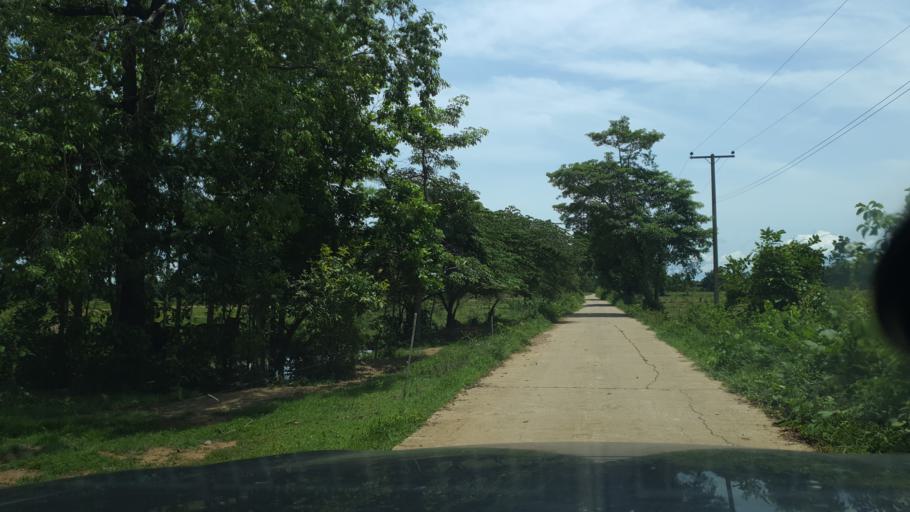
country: TH
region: Sukhothai
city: Ban Na
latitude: 17.0874
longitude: 99.6871
